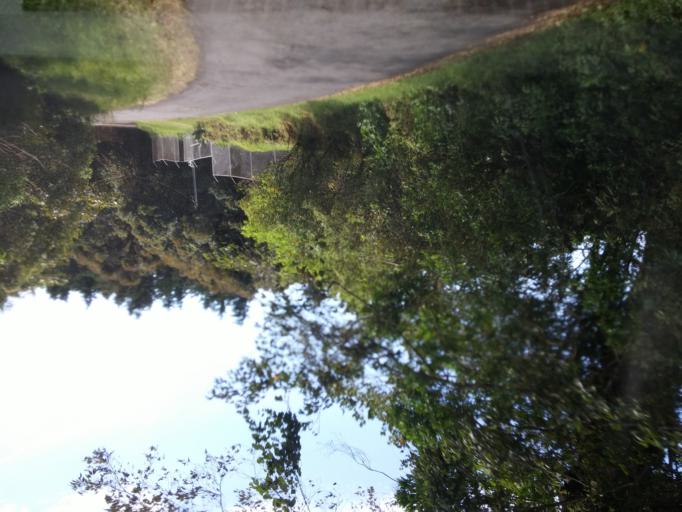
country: CR
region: Heredia
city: Santo Domingo
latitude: 10.0975
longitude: -84.1185
